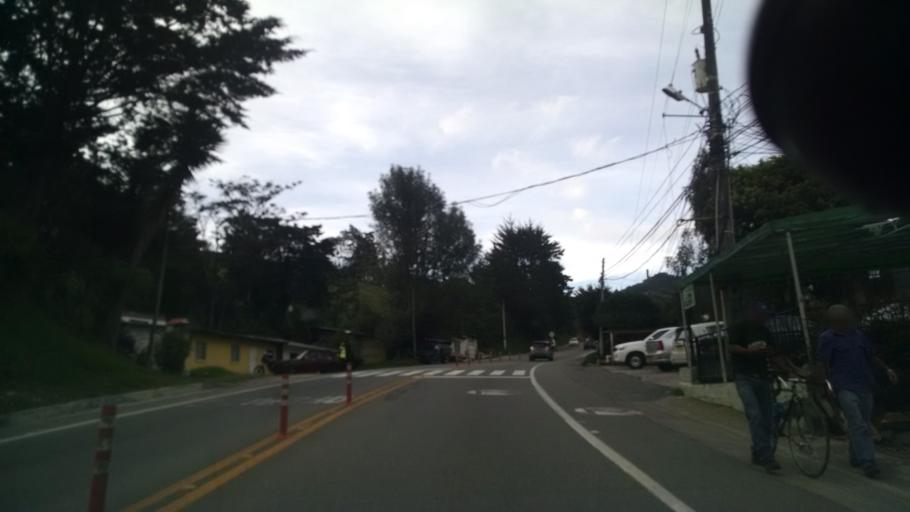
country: CO
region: Antioquia
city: El Retiro
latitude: 6.1173
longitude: -75.5008
